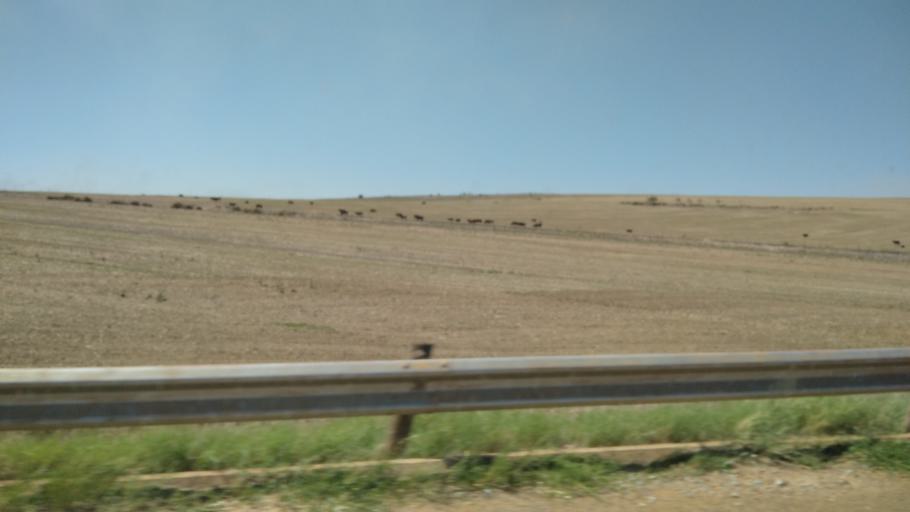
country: ZA
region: Western Cape
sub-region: West Coast District Municipality
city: Malmesbury
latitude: -33.3726
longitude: 18.6570
